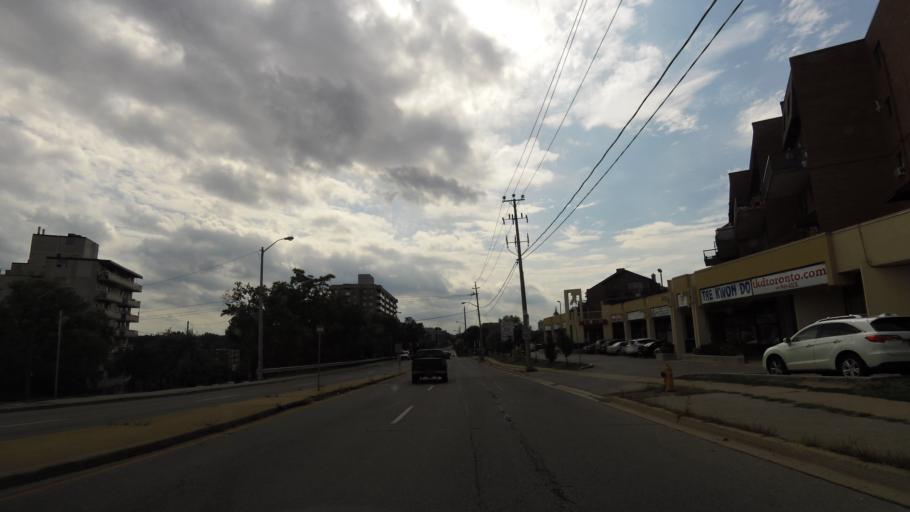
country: CA
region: Ontario
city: Etobicoke
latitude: 43.6649
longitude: -79.5018
